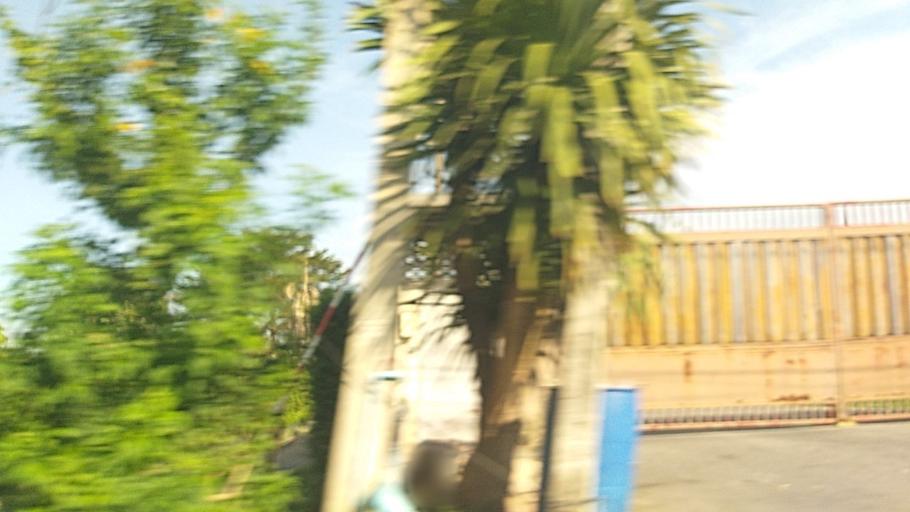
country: TH
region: Pathum Thani
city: Lam Luk Ka
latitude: 13.9743
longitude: 100.7287
